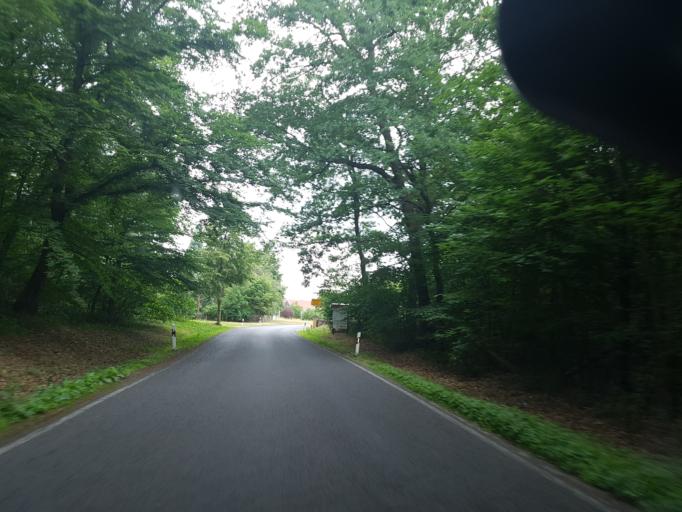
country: DE
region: Brandenburg
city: Hohenbucko
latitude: 51.7038
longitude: 13.4934
